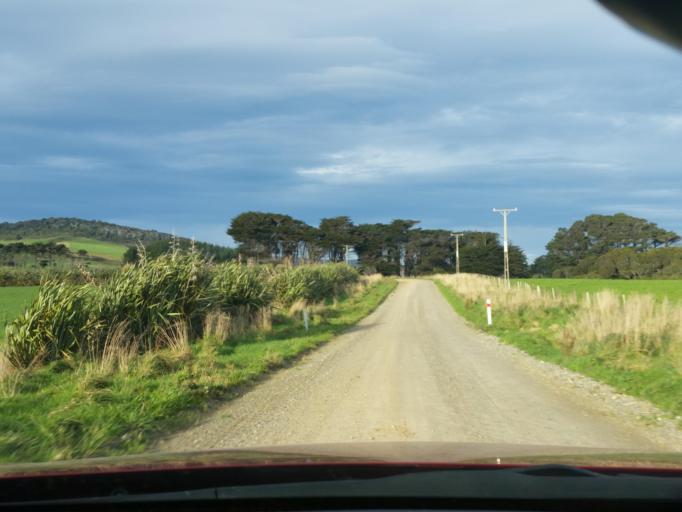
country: NZ
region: Southland
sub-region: Southland District
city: Riverton
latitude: -46.2964
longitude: 167.7581
